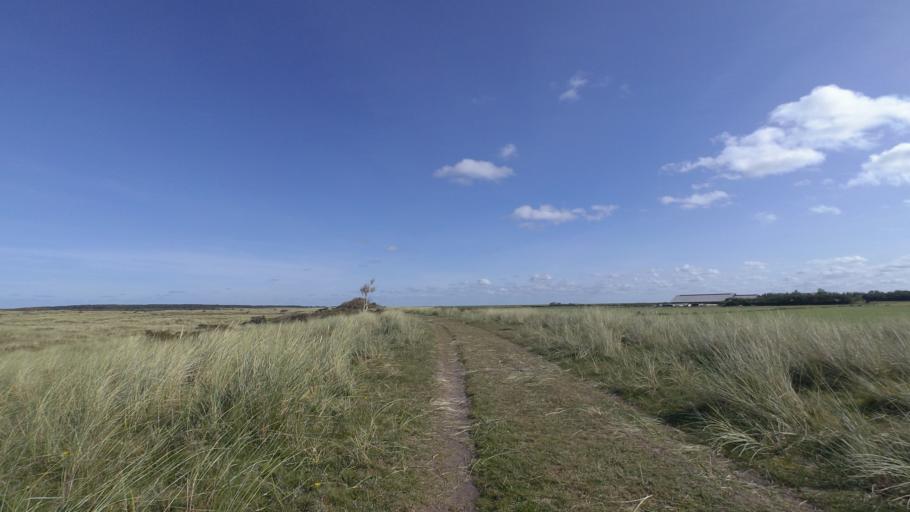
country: NL
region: Friesland
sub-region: Gemeente Ameland
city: Nes
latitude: 53.4508
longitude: 5.7240
